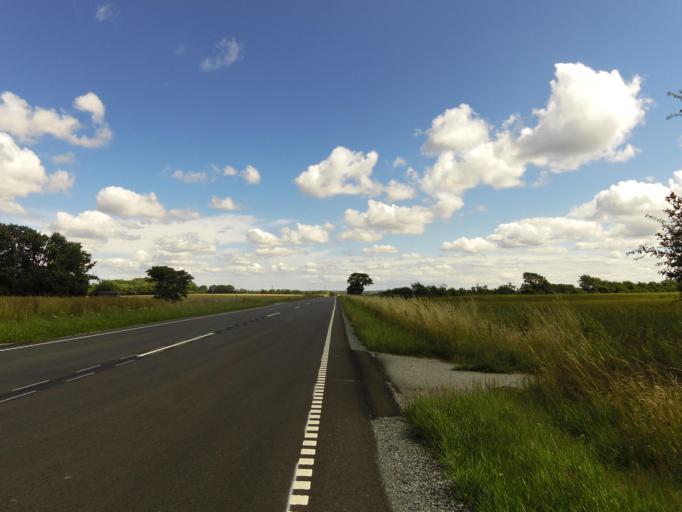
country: DK
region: South Denmark
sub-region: Haderslev Kommune
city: Gram
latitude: 55.3129
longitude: 9.1204
